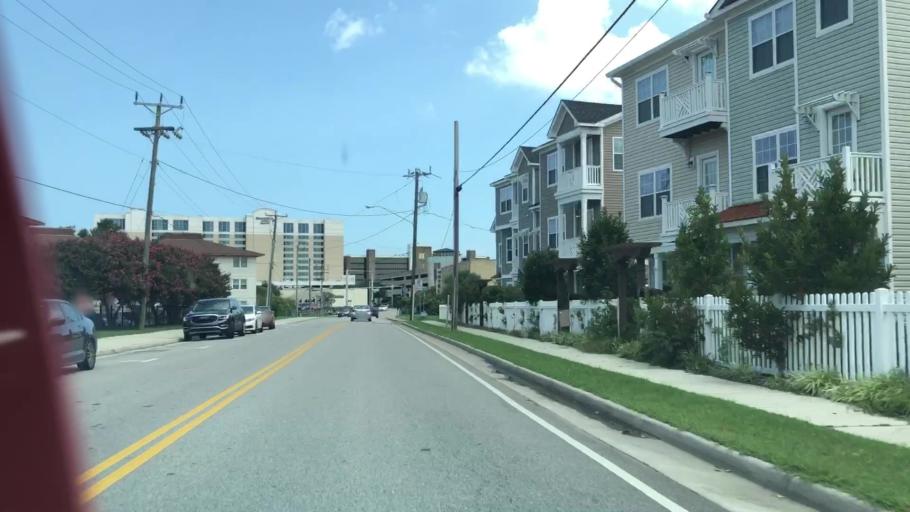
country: US
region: Virginia
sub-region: City of Virginia Beach
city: Virginia Beach
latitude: 36.8376
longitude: -75.9763
